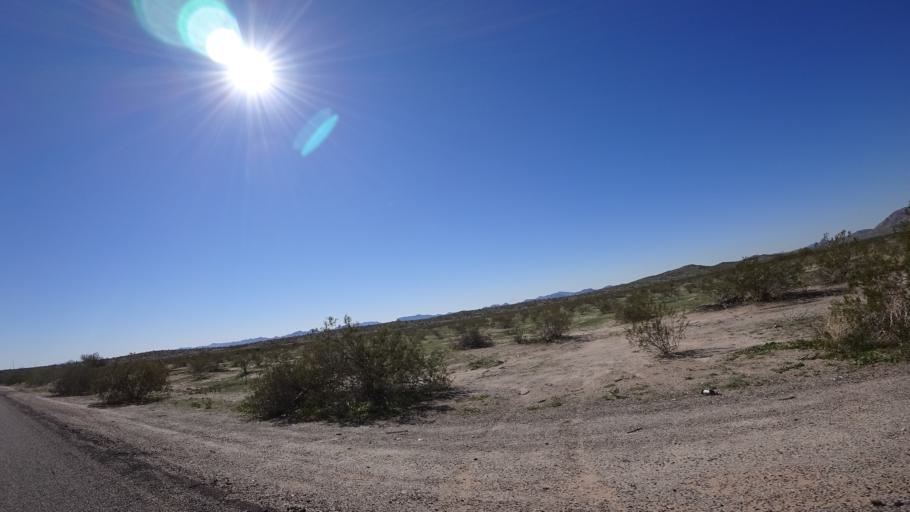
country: US
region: Arizona
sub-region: Maricopa County
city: Buckeye
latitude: 33.3013
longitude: -112.4576
